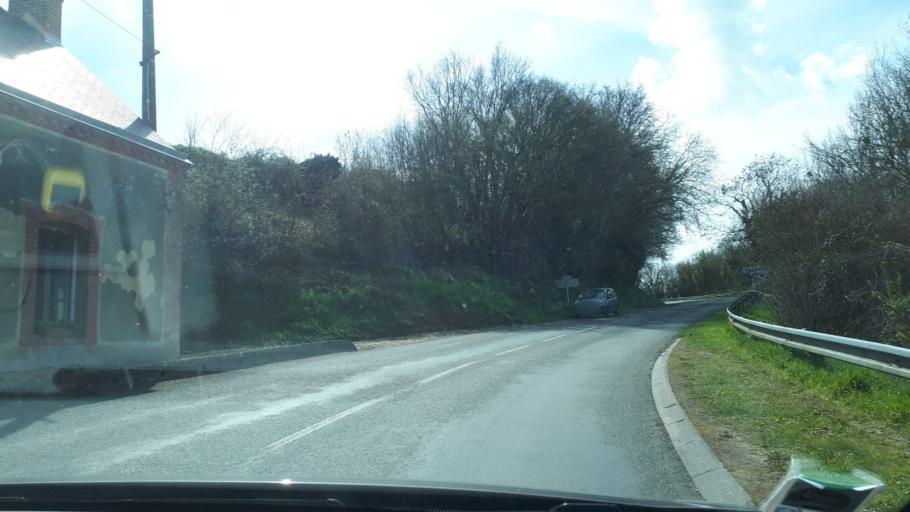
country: FR
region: Pays de la Loire
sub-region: Departement de la Sarthe
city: Bouloire
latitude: 47.9026
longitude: 0.5774
